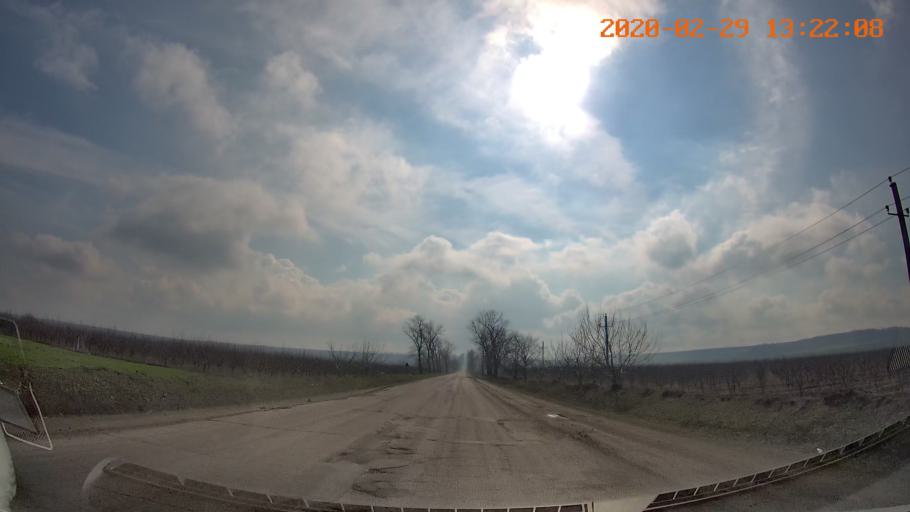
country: MD
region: Telenesti
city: Camenca
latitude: 47.9639
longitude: 28.6285
